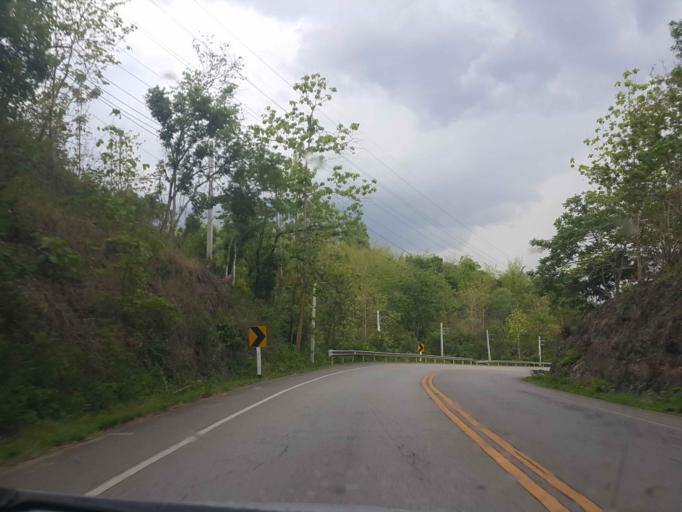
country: TH
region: Phrae
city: Den Chai
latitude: 17.9659
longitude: 100.0535
